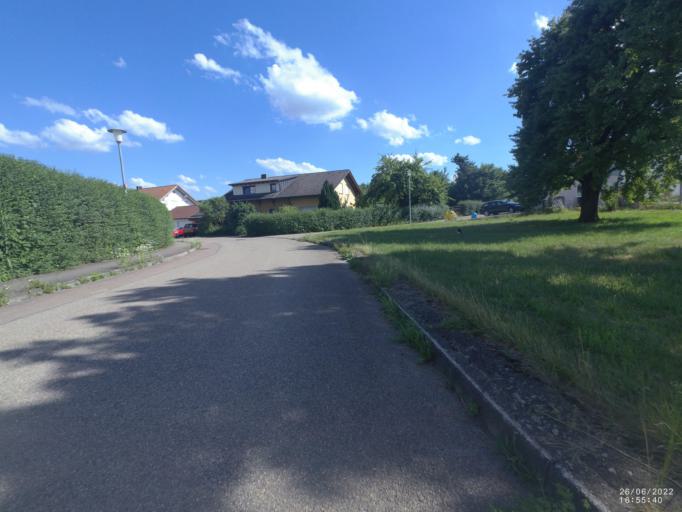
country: DE
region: Baden-Wuerttemberg
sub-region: Regierungsbezirk Stuttgart
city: Bohmenkirch
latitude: 48.6400
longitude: 9.9547
